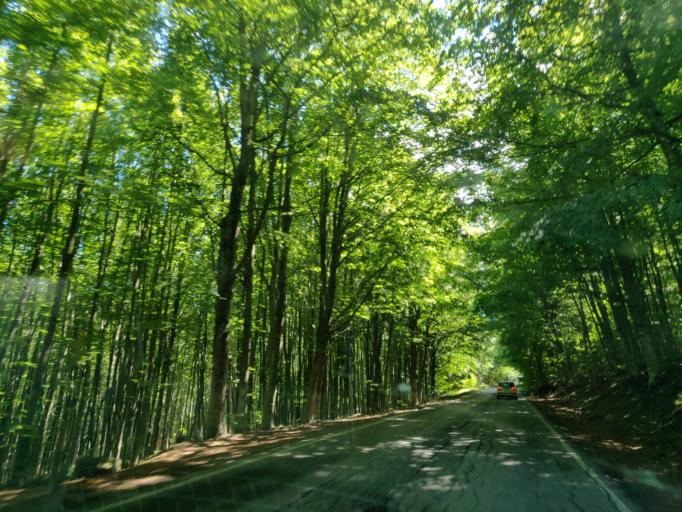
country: IT
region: Tuscany
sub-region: Provincia di Siena
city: Abbadia San Salvatore
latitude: 42.9032
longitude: 11.6224
